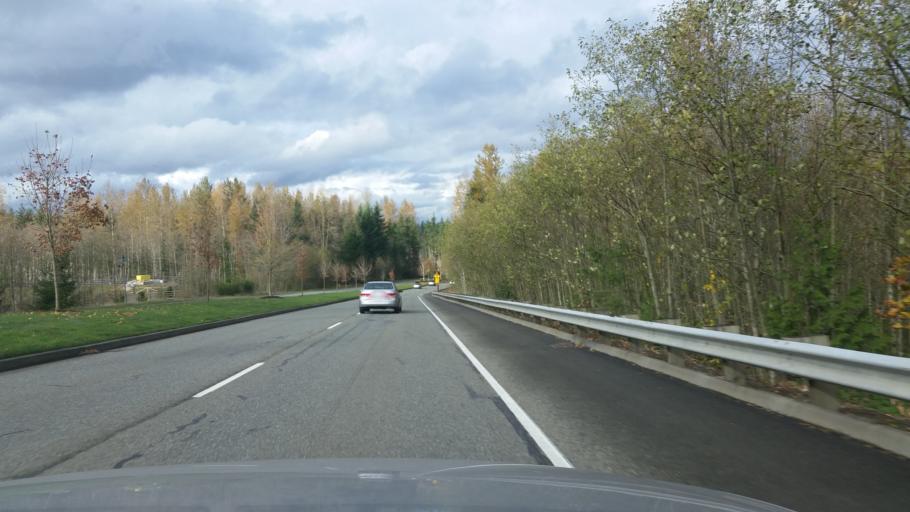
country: US
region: Washington
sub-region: King County
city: Fall City
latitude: 47.5210
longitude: -121.8794
